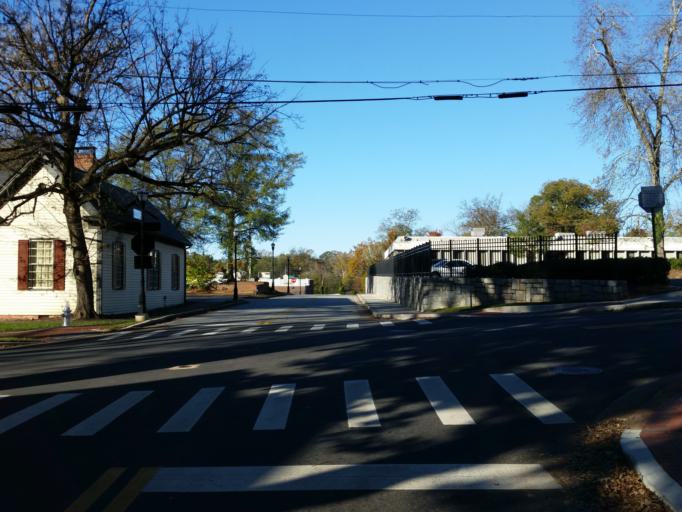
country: US
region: Georgia
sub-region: Cobb County
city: Marietta
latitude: 33.9521
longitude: -84.5447
